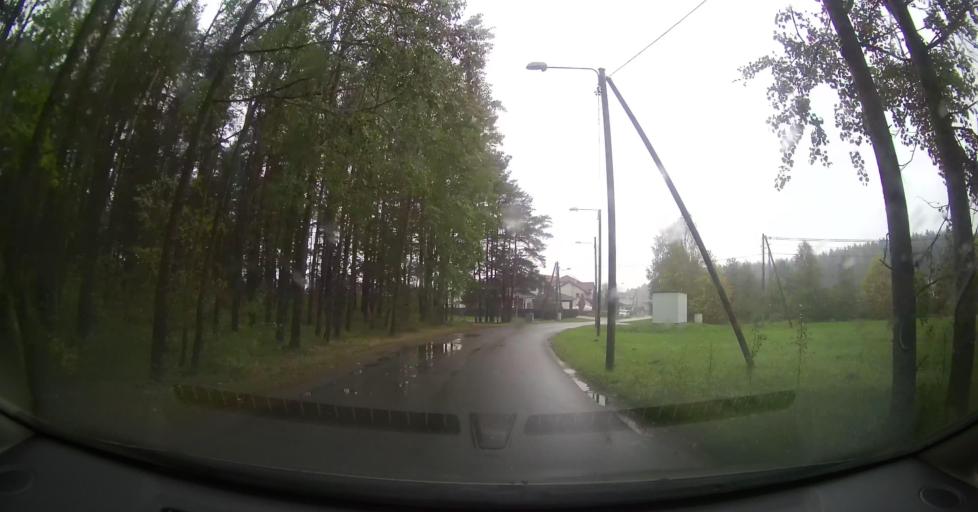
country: EE
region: Tartu
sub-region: Tartu linn
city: Tartu
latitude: 58.3587
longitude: 26.7940
